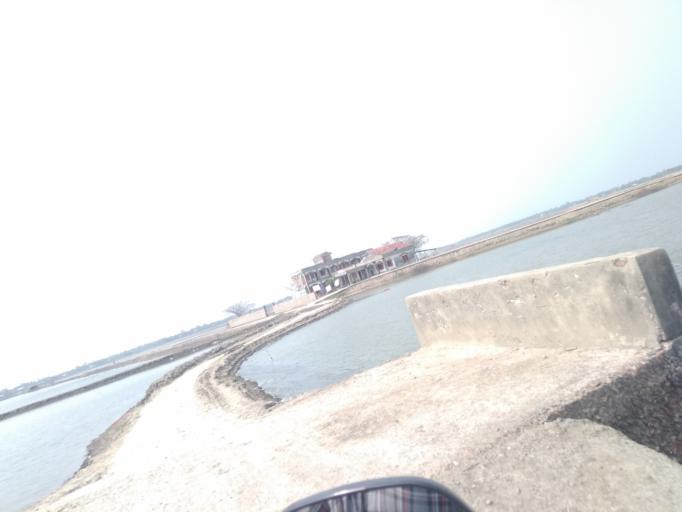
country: IN
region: West Bengal
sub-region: North 24 Parganas
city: Taki
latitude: 22.3448
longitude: 89.2298
